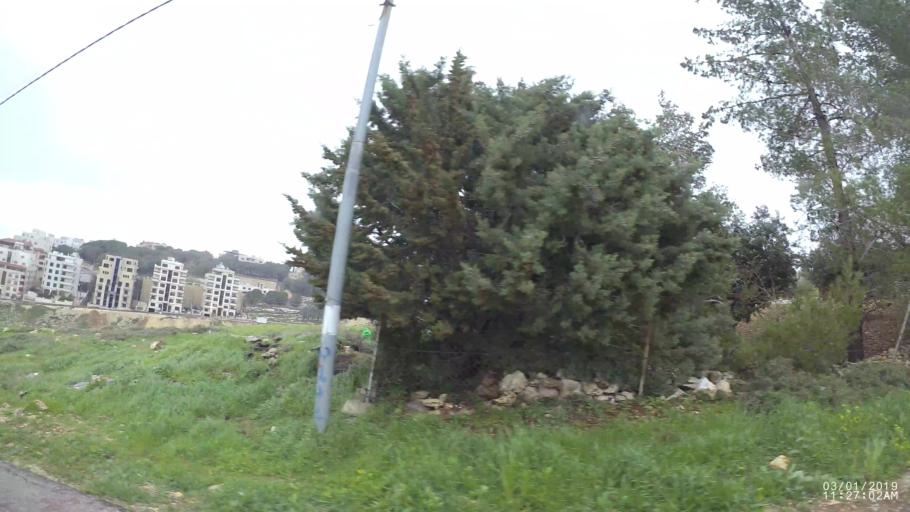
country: JO
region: Amman
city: Umm as Summaq
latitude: 31.9157
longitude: 35.8649
